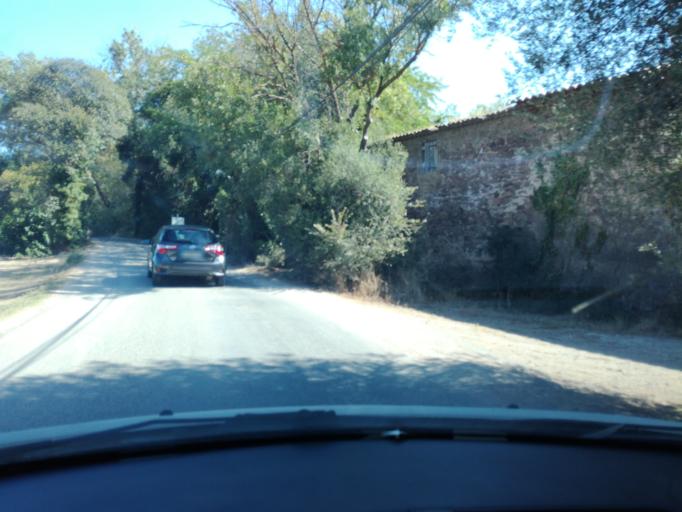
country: FR
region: Provence-Alpes-Cote d'Azur
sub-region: Departement du Var
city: La Crau
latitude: 43.1601
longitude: 6.0670
